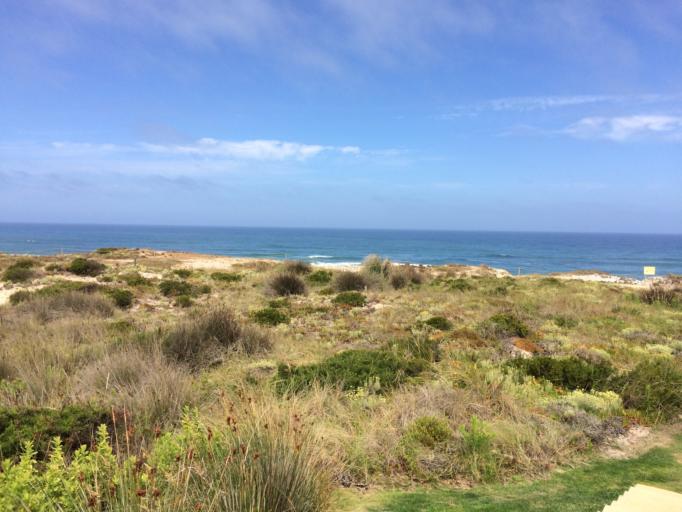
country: PT
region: Leiria
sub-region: Peniche
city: Atouguia da Baleia
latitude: 39.3913
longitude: -9.2883
